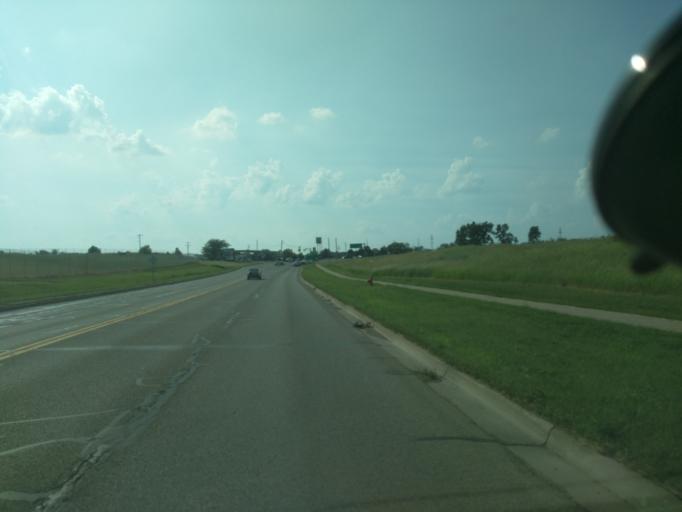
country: US
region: Michigan
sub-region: Jackson County
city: Jackson
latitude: 42.2661
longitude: -84.4504
